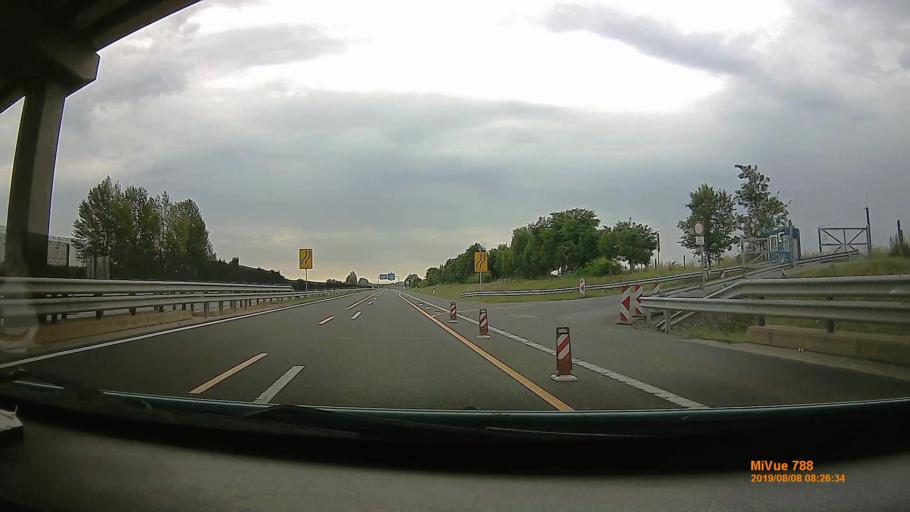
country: HU
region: Hajdu-Bihar
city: Hajduboszormeny
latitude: 47.5774
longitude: 21.5314
